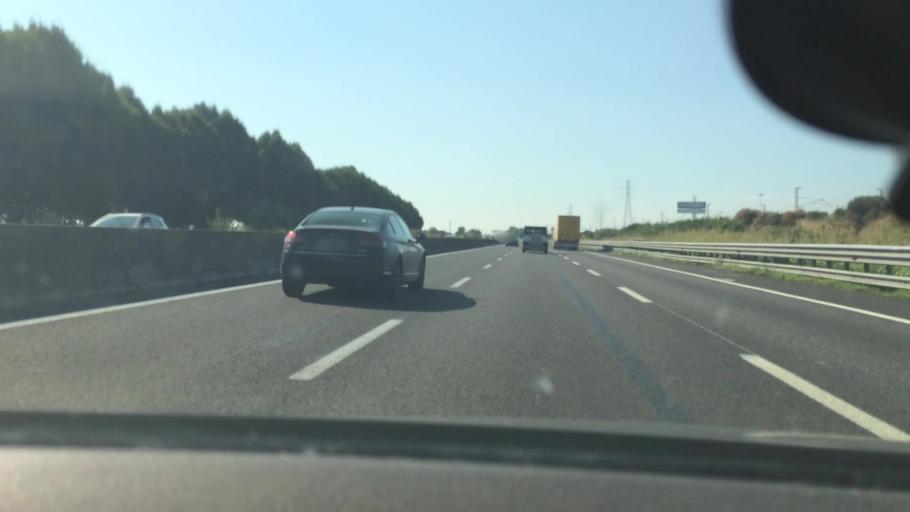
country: IT
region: Lombardy
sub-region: Provincia di Lodi
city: Senna Lodigiana
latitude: 45.1638
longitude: 9.6045
